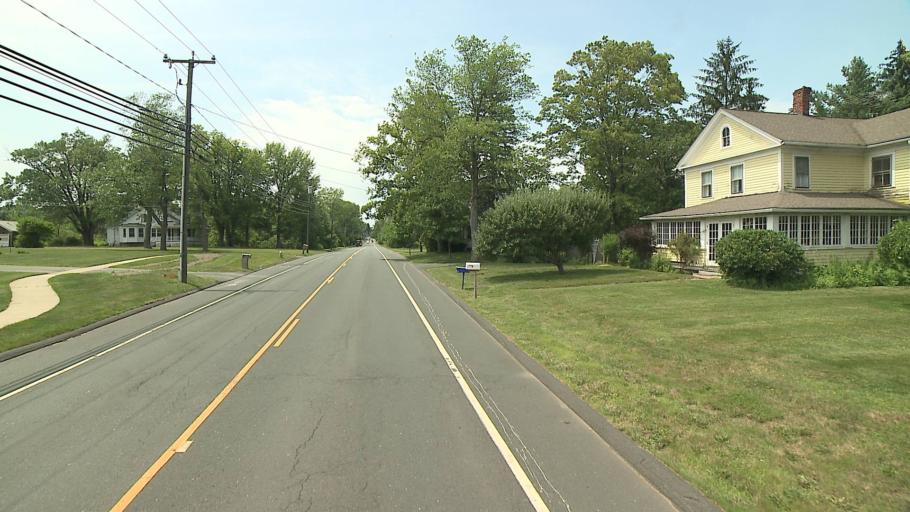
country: US
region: Connecticut
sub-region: Hartford County
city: Suffield Depot
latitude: 41.9794
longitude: -72.6393
